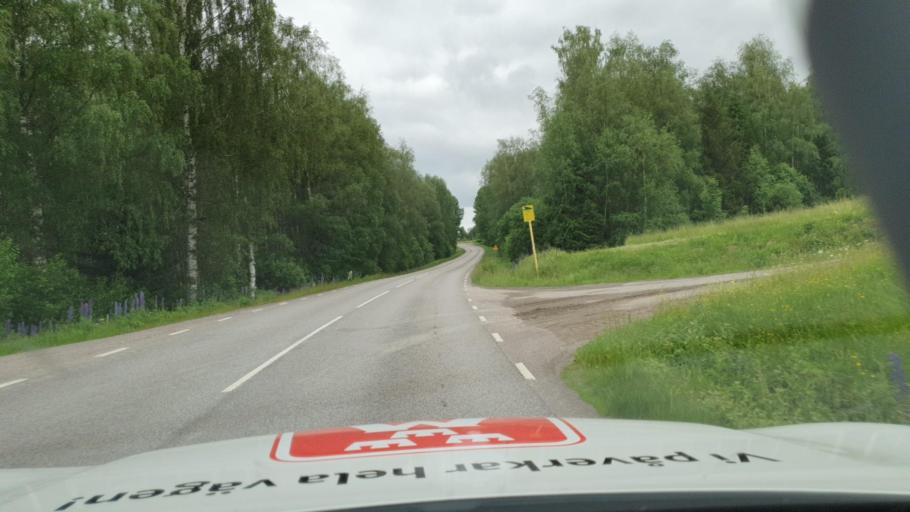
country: SE
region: Vaermland
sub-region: Sunne Kommun
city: Sunne
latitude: 59.8008
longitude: 13.0517
